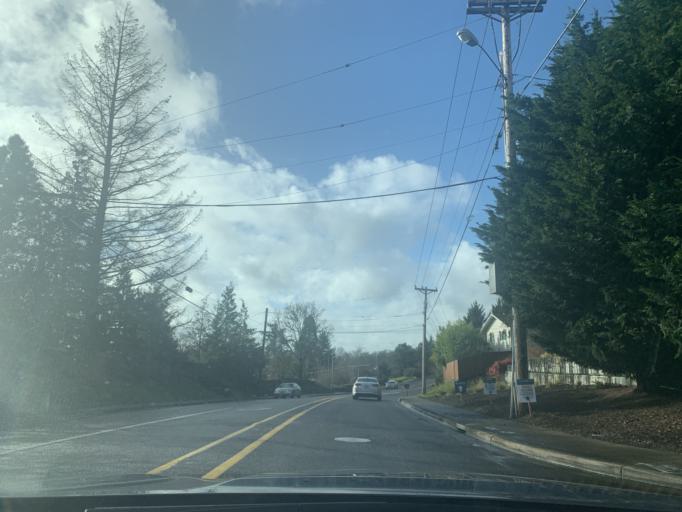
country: US
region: Oregon
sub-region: Washington County
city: King City
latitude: 45.4060
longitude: -122.8074
